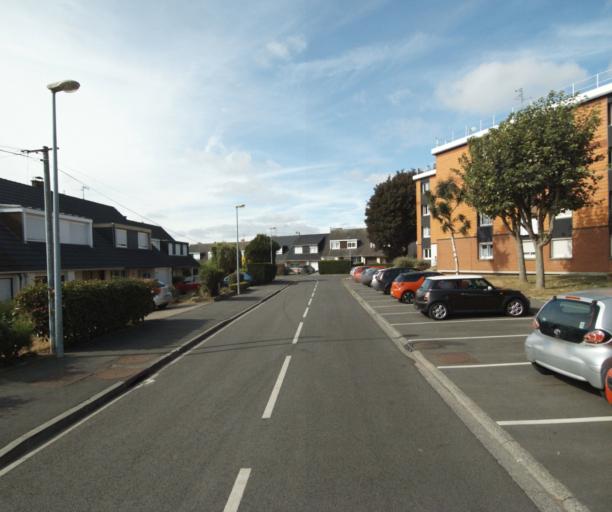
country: FR
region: Nord-Pas-de-Calais
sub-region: Departement du Nord
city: Linselles
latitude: 50.7321
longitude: 3.0803
